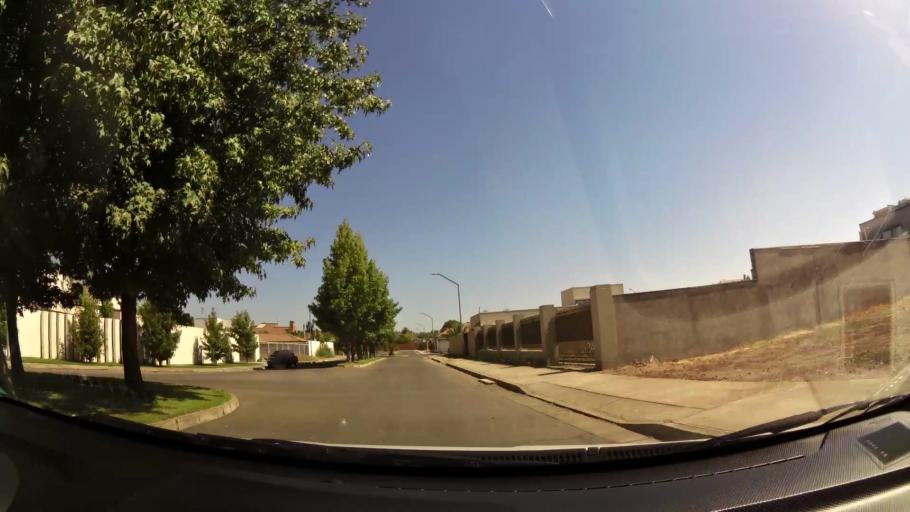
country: CL
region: Maule
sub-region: Provincia de Talca
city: Talca
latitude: -35.4362
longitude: -71.6144
